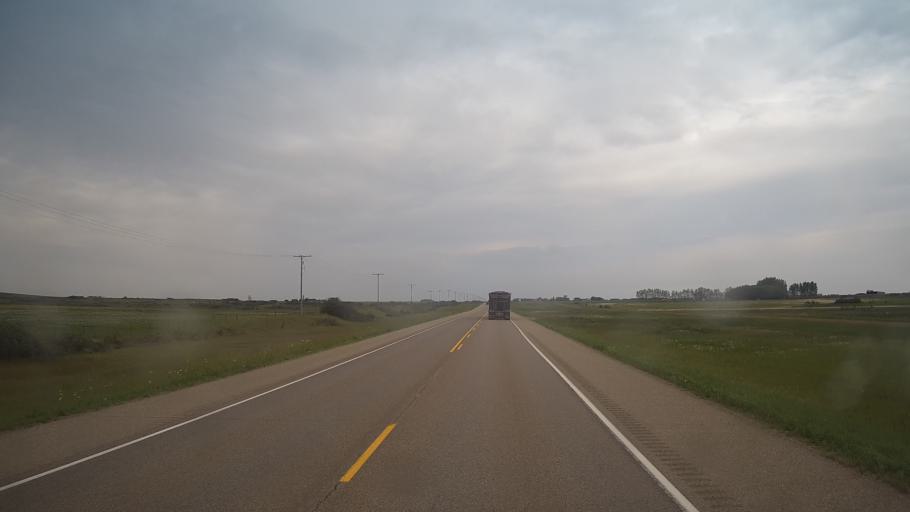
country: CA
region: Saskatchewan
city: Langham
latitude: 52.1289
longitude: -107.1707
